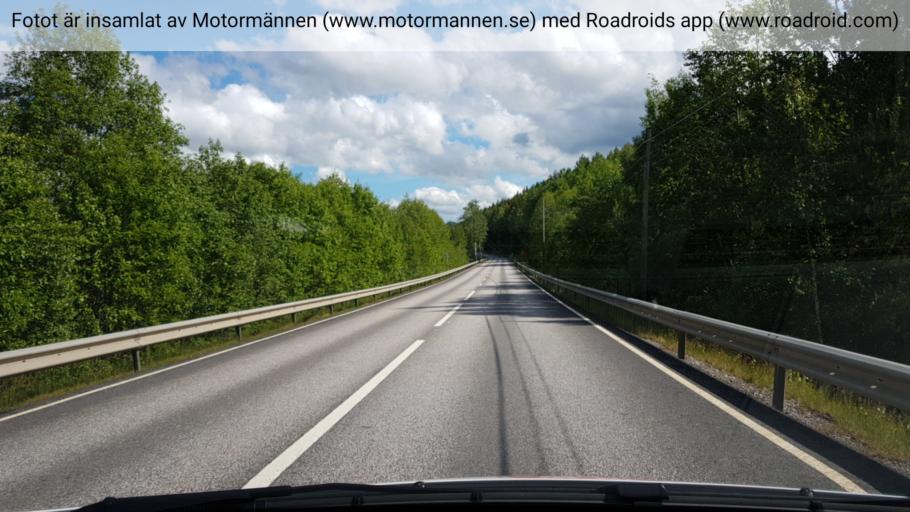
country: SE
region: Kalmar
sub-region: Vasterviks Kommun
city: Overum
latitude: 58.0091
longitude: 16.2660
